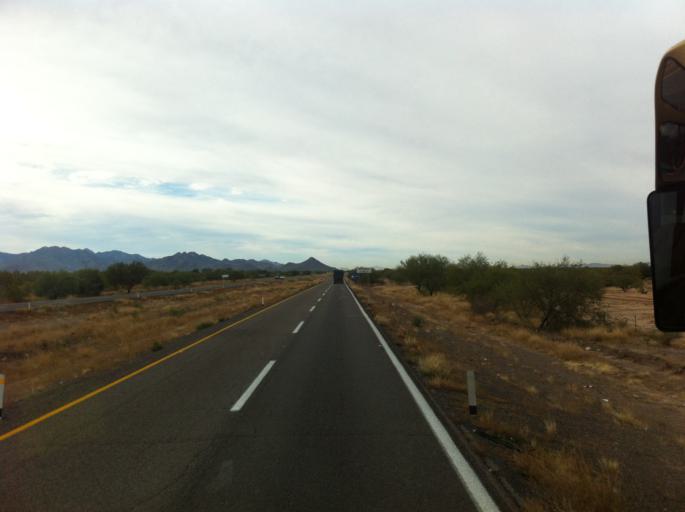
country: MX
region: Sonora
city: Hermosillo
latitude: 28.7198
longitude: -110.9818
